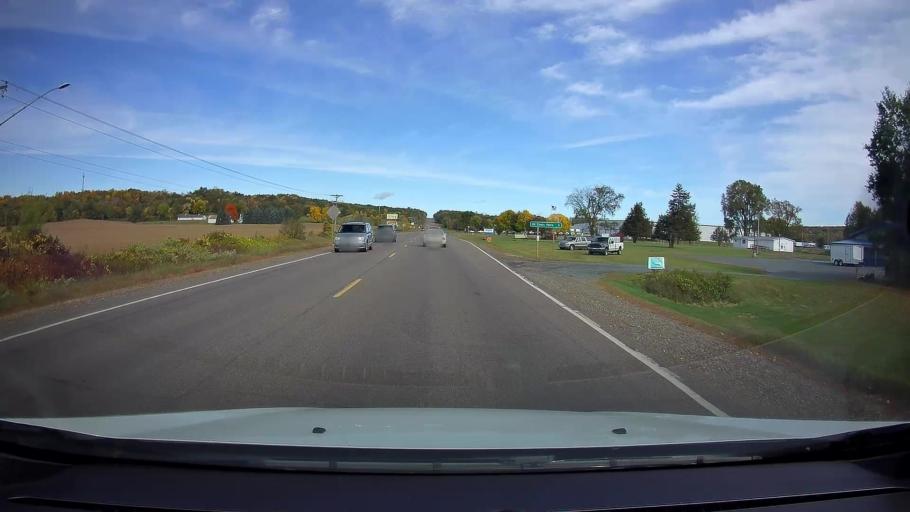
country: US
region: Wisconsin
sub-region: Polk County
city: Saint Croix Falls
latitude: 45.3600
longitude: -92.6366
